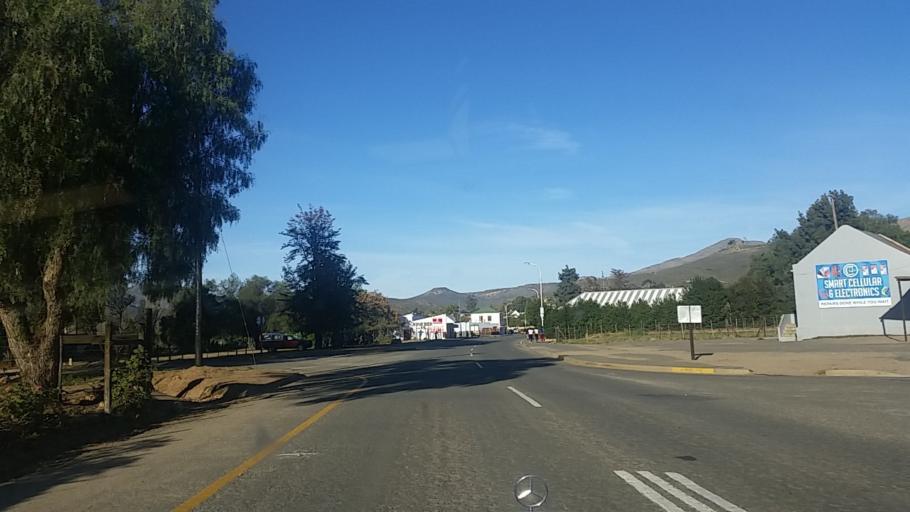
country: ZA
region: Western Cape
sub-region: Eden District Municipality
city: Knysna
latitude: -33.6591
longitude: 23.1173
